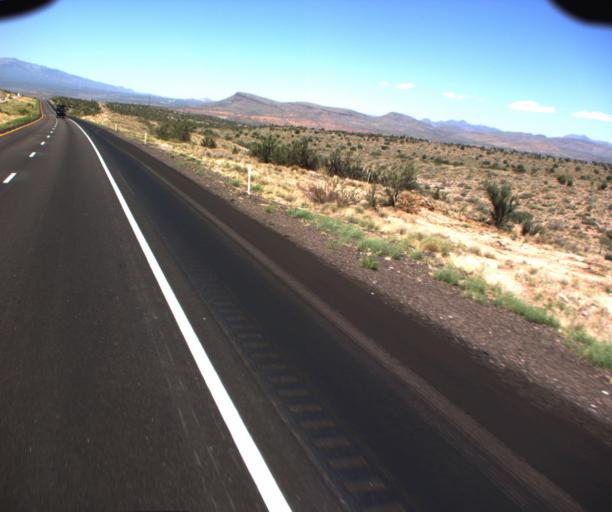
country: US
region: Arizona
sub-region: Mohave County
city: Peach Springs
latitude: 35.1624
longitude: -113.5847
